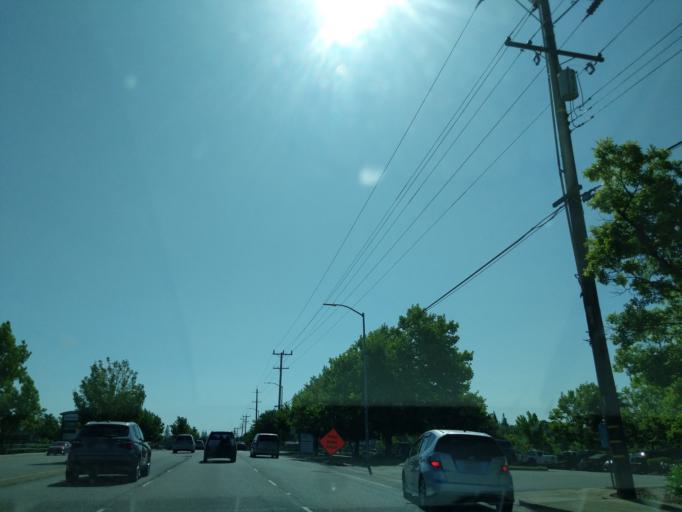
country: US
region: California
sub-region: Sacramento County
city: Citrus Heights
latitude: 38.6782
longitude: -121.2957
